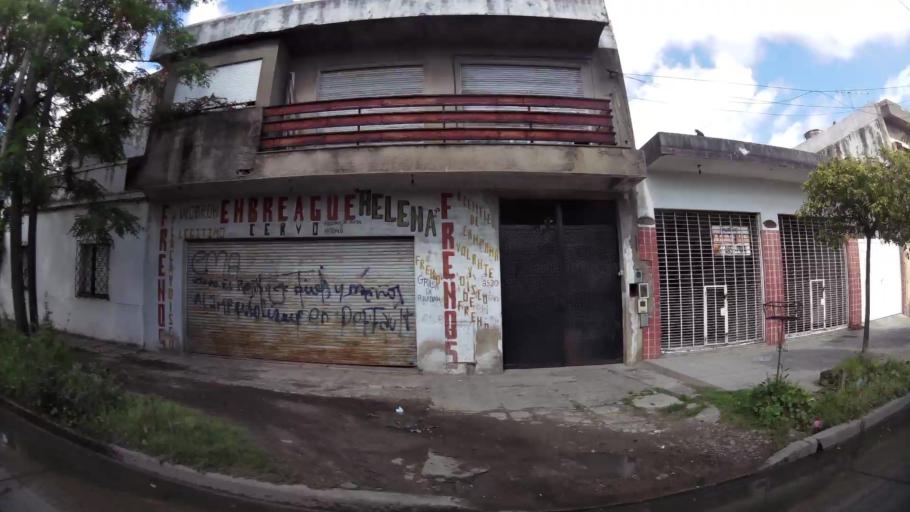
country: AR
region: Buenos Aires
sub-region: Partido de Lanus
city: Lanus
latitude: -34.6812
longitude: -58.4301
